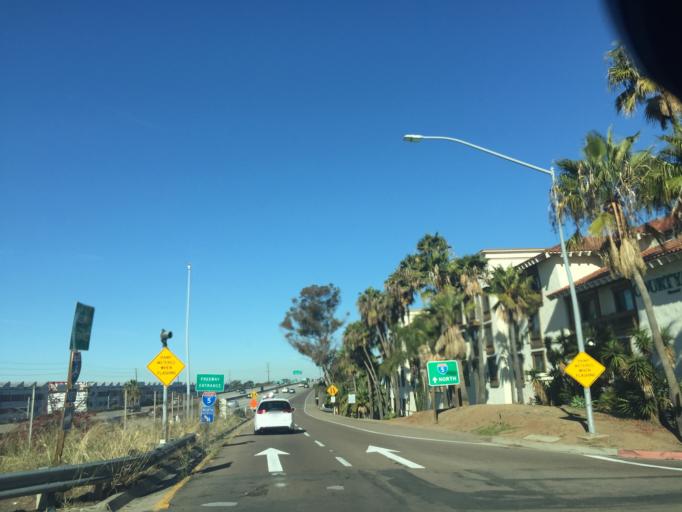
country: US
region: California
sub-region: San Diego County
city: San Diego
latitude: 32.7493
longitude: -117.1949
